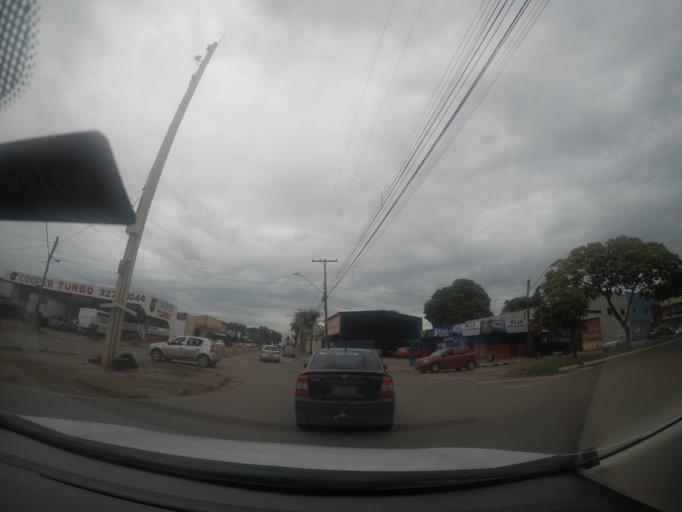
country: BR
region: Goias
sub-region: Goiania
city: Goiania
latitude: -16.6669
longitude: -49.3237
